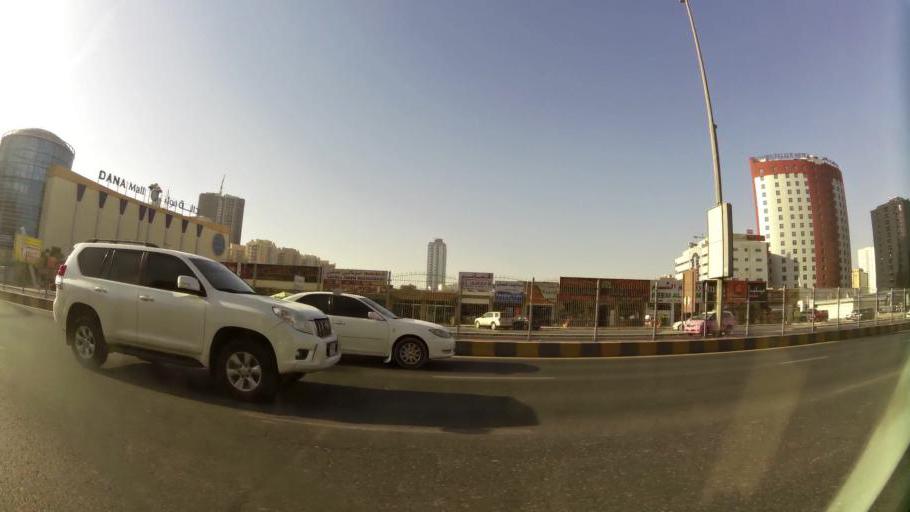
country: AE
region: Ajman
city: Ajman
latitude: 25.3890
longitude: 55.4596
